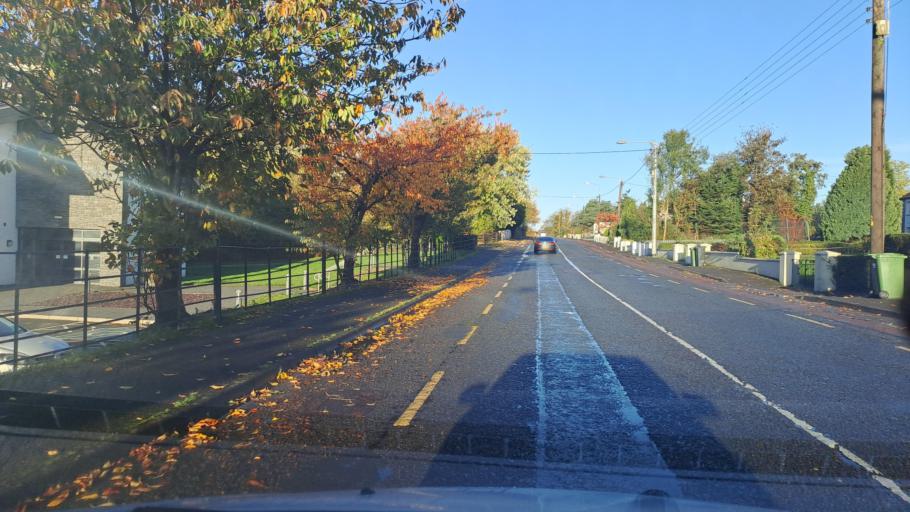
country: IE
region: Ulster
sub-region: An Cabhan
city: Cootehill
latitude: 54.0718
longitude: -7.0710
